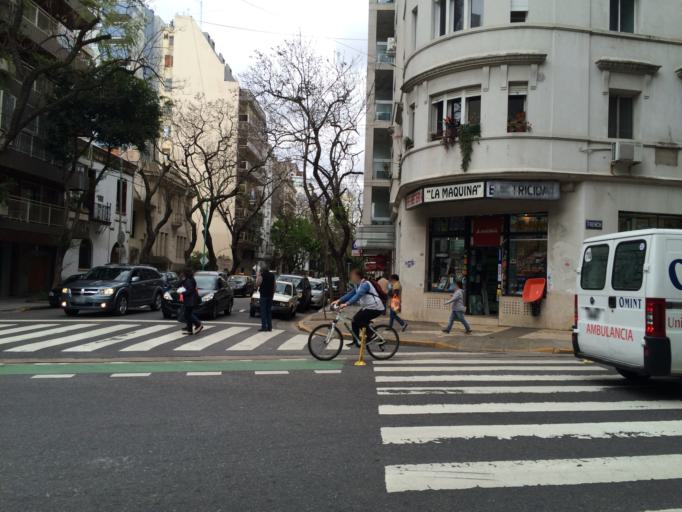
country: AR
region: Buenos Aires F.D.
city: Retiro
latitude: -34.5888
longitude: -58.4032
